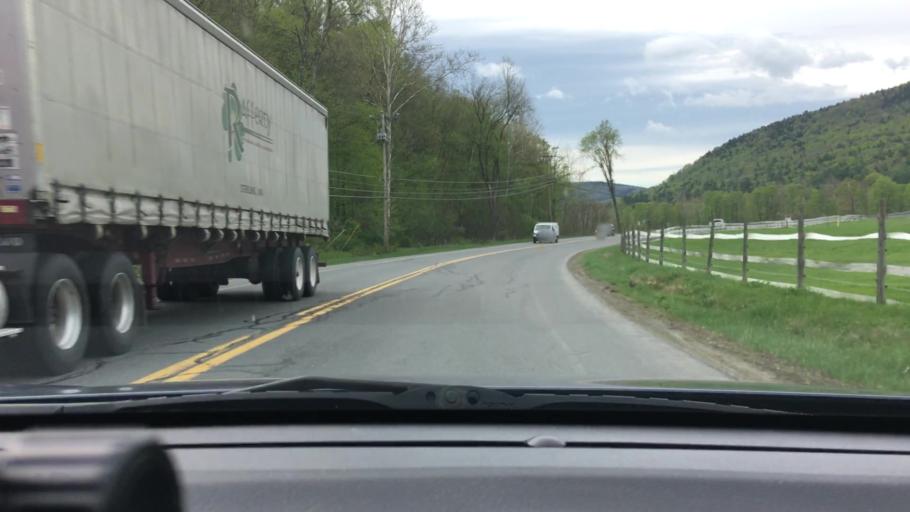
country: US
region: Vermont
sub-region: Windham County
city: Newfane
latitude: 43.0272
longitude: -72.6570
